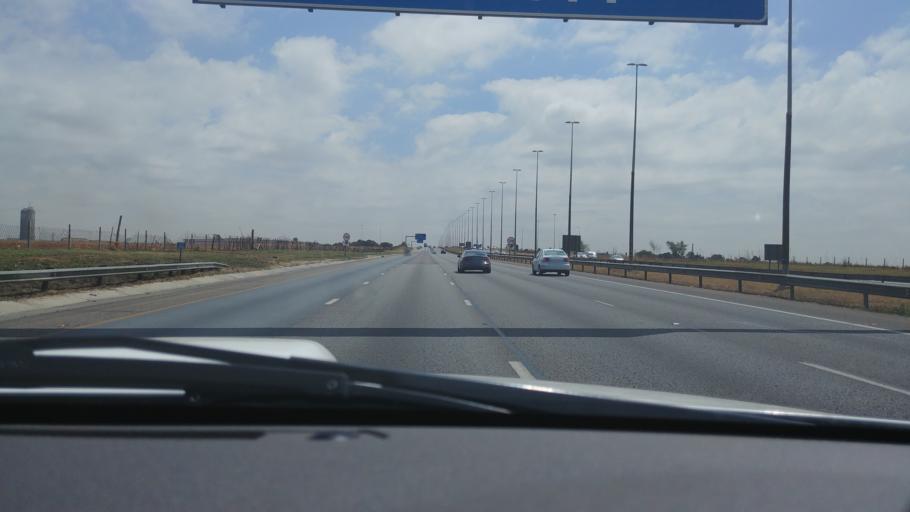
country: ZA
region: Gauteng
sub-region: Ekurhuleni Metropolitan Municipality
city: Tembisa
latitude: -26.0379
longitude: 28.2707
